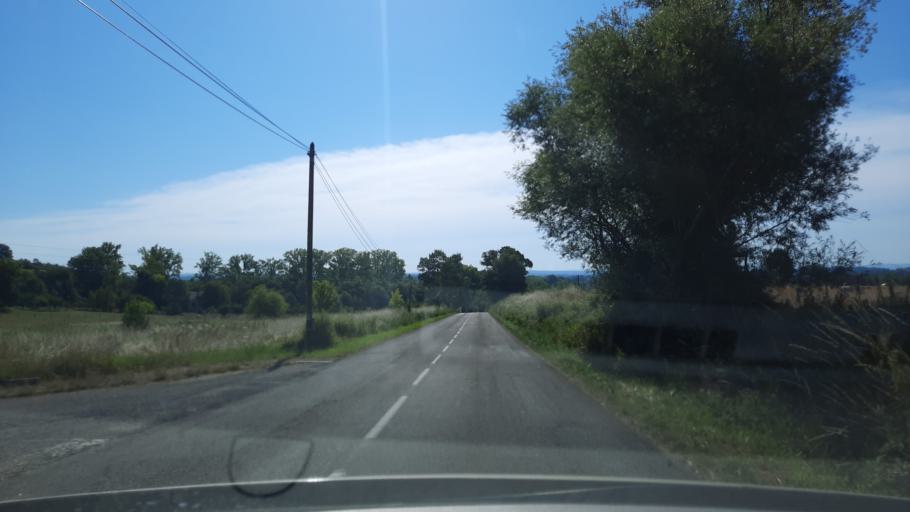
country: FR
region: Midi-Pyrenees
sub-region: Departement du Tarn-et-Garonne
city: Caussade
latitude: 44.1694
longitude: 1.5197
